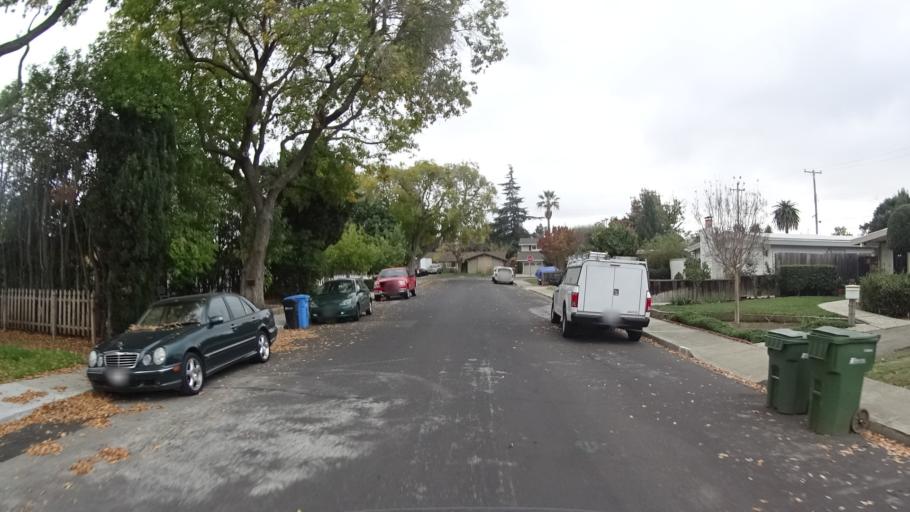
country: US
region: California
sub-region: Santa Clara County
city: Santa Clara
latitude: 37.3335
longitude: -121.9813
